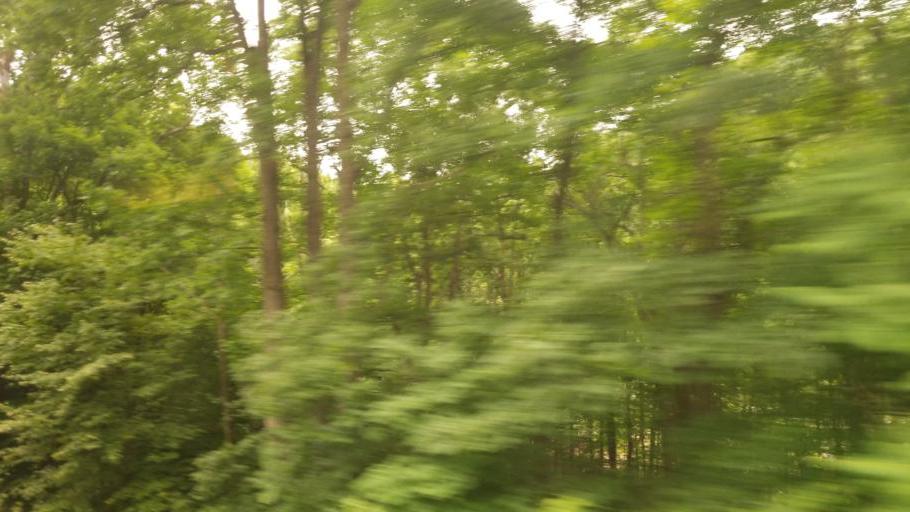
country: US
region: Pennsylvania
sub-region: Fayette County
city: South Connellsville
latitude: 39.9032
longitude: -79.4739
